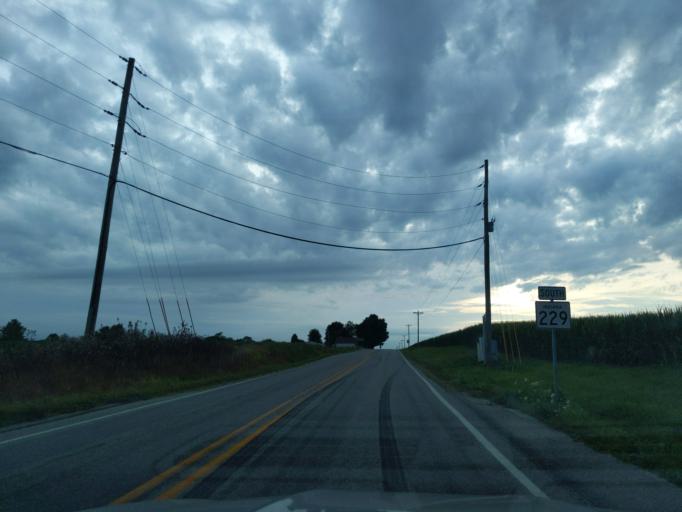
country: US
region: Indiana
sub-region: Ripley County
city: Osgood
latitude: 39.1962
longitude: -85.2782
